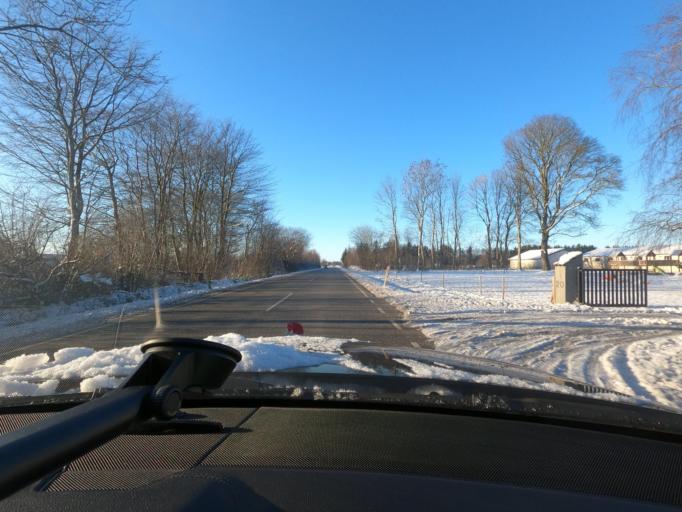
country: DK
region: South Denmark
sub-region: Aabenraa Kommune
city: Rodekro
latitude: 55.0743
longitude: 9.3105
